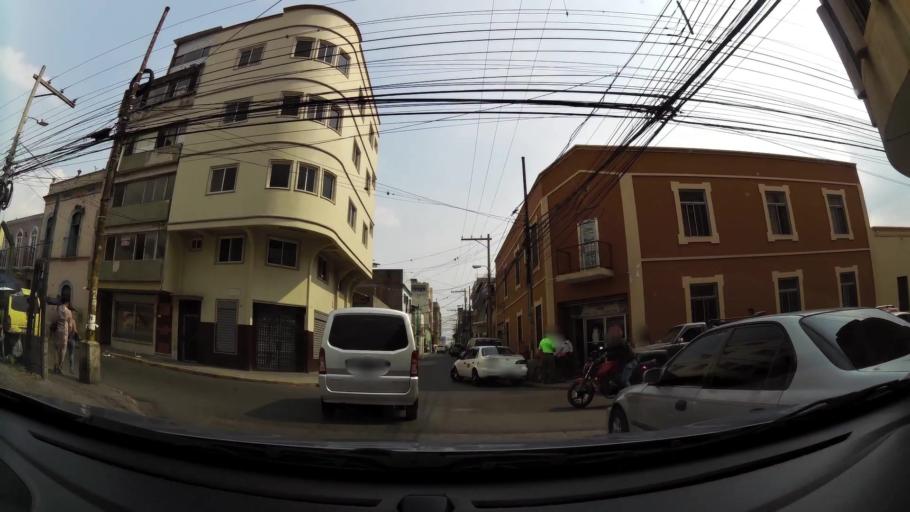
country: HN
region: Francisco Morazan
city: Tegucigalpa
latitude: 14.1088
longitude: -87.2074
